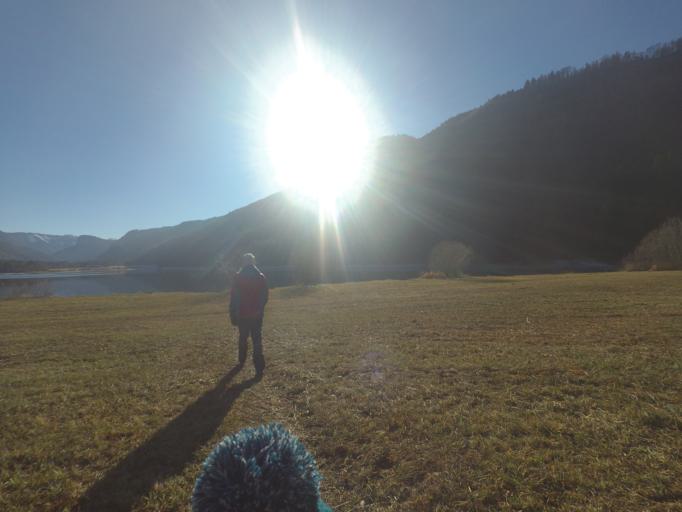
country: AT
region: Salzburg
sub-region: Politischer Bezirk Salzburg-Umgebung
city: Faistenau
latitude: 47.7520
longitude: 13.2424
